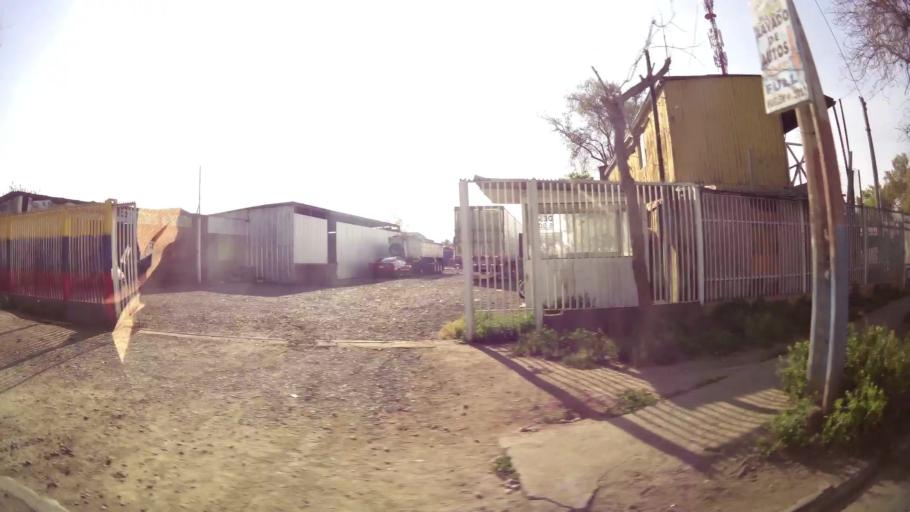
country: CL
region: Santiago Metropolitan
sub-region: Provincia de Santiago
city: Lo Prado
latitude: -33.4145
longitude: -70.7424
